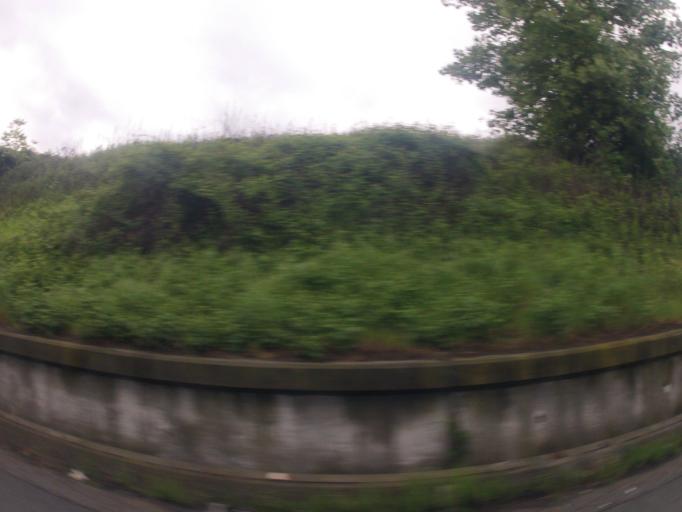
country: IT
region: Piedmont
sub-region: Provincia di Torino
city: La Loggia
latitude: 44.9464
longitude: 7.6790
